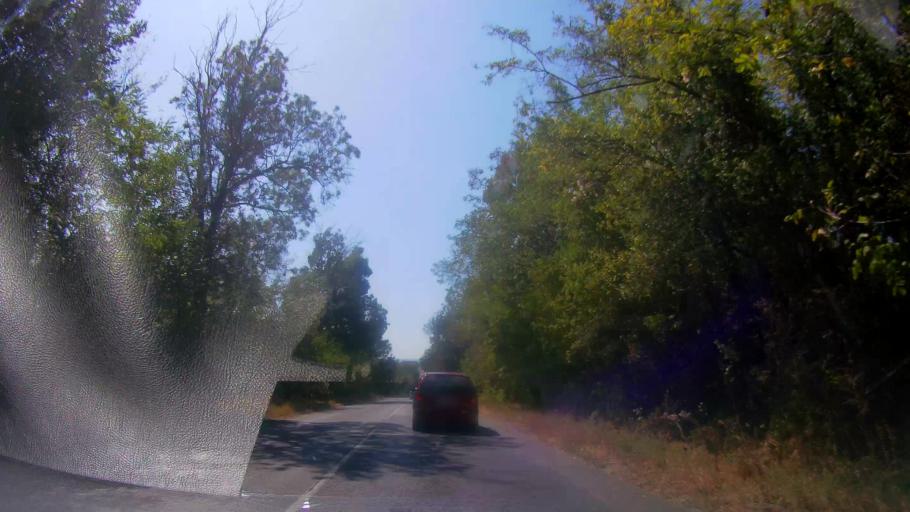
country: BG
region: Veliko Turnovo
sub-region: Obshtina Gorna Oryakhovitsa
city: Purvomaytsi
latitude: 43.2447
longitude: 25.6437
